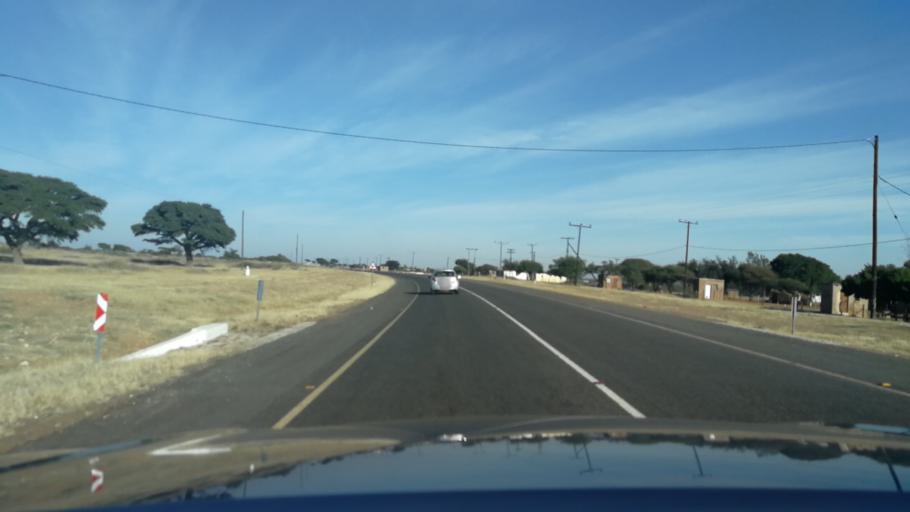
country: BW
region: South East
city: Janeng
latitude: -25.4679
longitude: 25.5412
